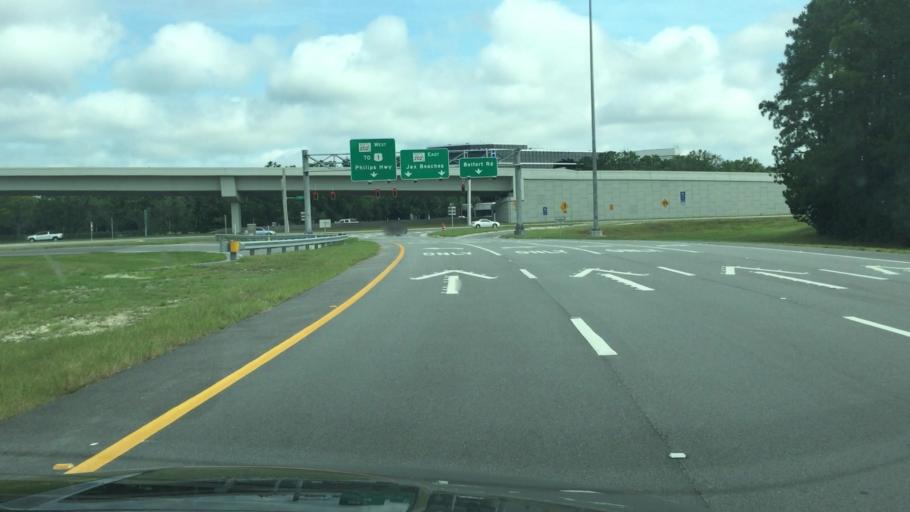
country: US
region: Florida
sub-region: Duval County
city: Jacksonville
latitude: 30.2483
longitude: -81.5910
